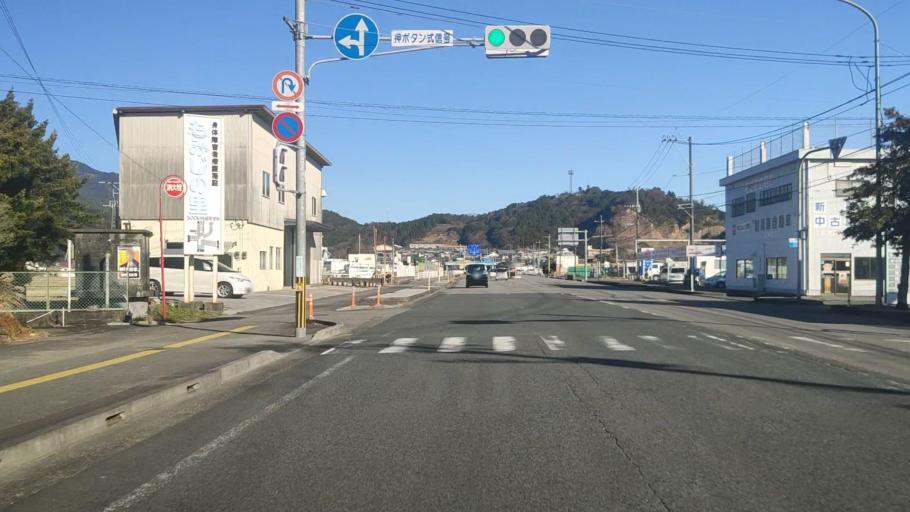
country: JP
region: Miyazaki
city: Nobeoka
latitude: 32.6053
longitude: 131.6828
